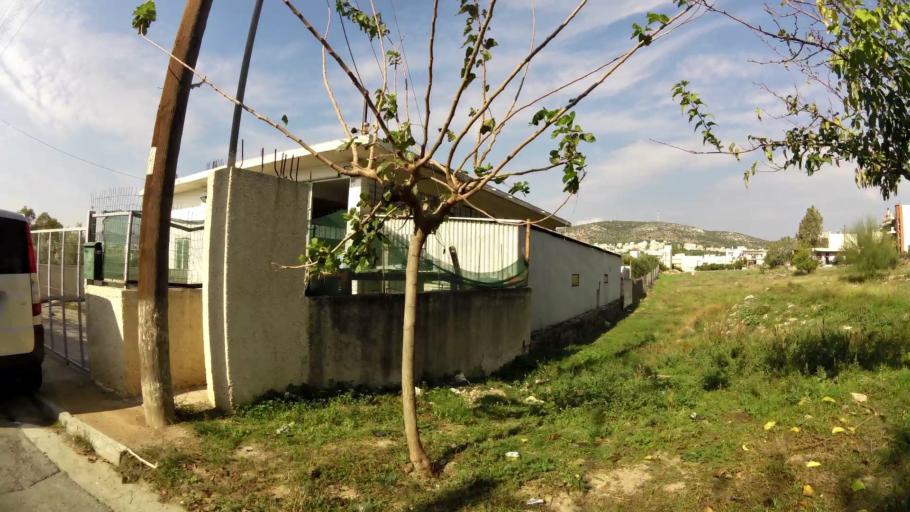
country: GR
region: Attica
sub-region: Nomarchia Athinas
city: Kamateron
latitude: 38.0492
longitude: 23.7099
